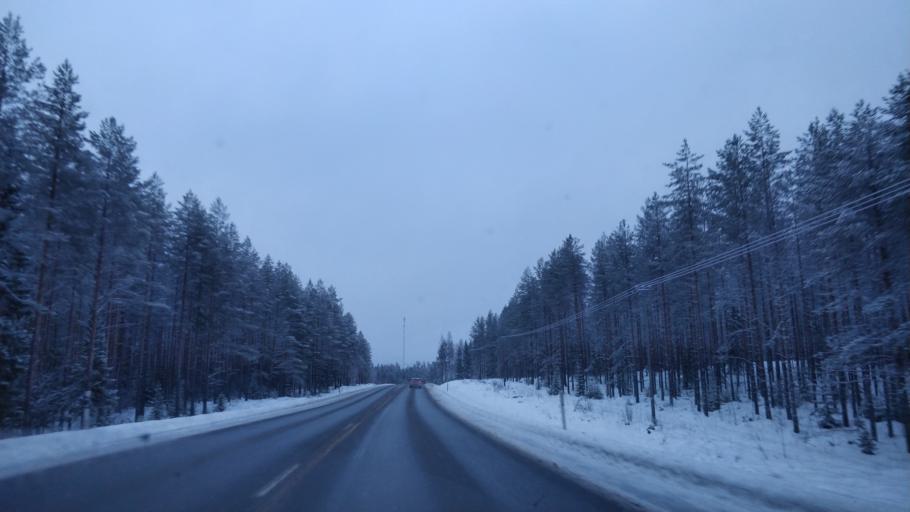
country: FI
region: Central Finland
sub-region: Saarijaervi-Viitasaari
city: Viitasaari
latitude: 63.1976
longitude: 25.6964
